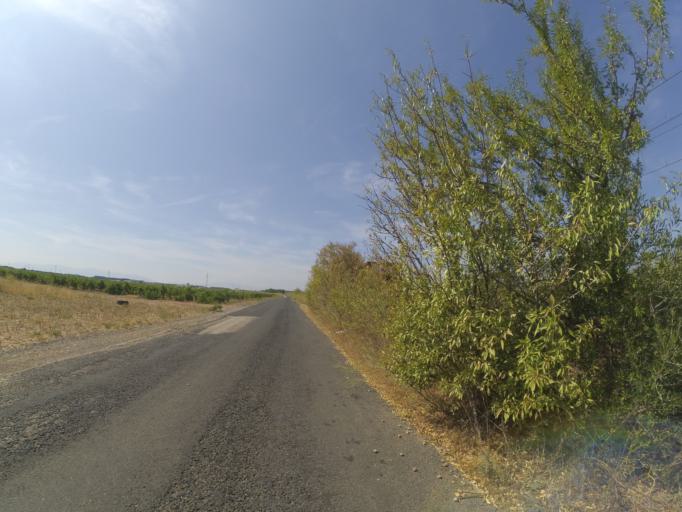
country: FR
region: Languedoc-Roussillon
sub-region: Departement des Pyrenees-Orientales
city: Salses-le-Chateau
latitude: 42.7982
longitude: 2.9006
